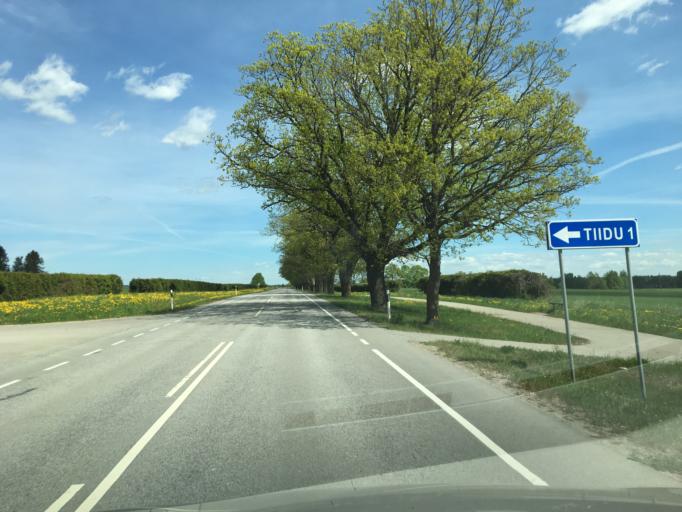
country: EE
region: Vorumaa
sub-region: Antsla vald
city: Vana-Antsla
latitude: 57.9169
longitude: 26.3086
